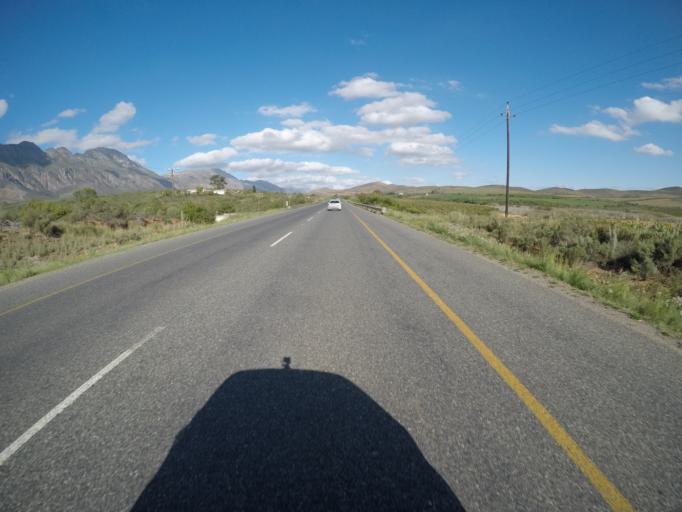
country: ZA
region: Western Cape
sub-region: Cape Winelands District Municipality
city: Ashton
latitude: -33.8546
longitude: 20.1055
